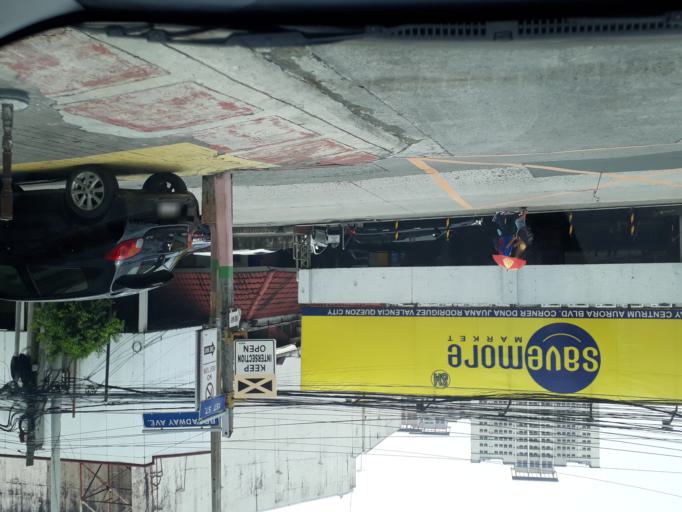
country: PH
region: Metro Manila
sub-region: San Juan
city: San Juan
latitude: 14.6120
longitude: 121.0331
